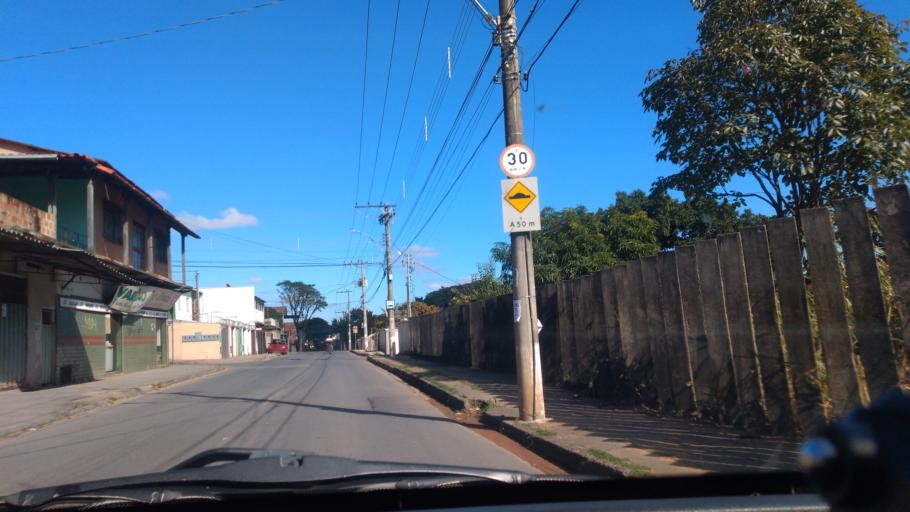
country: BR
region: Minas Gerais
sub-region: Santa Luzia
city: Santa Luzia
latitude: -19.8107
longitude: -43.9426
